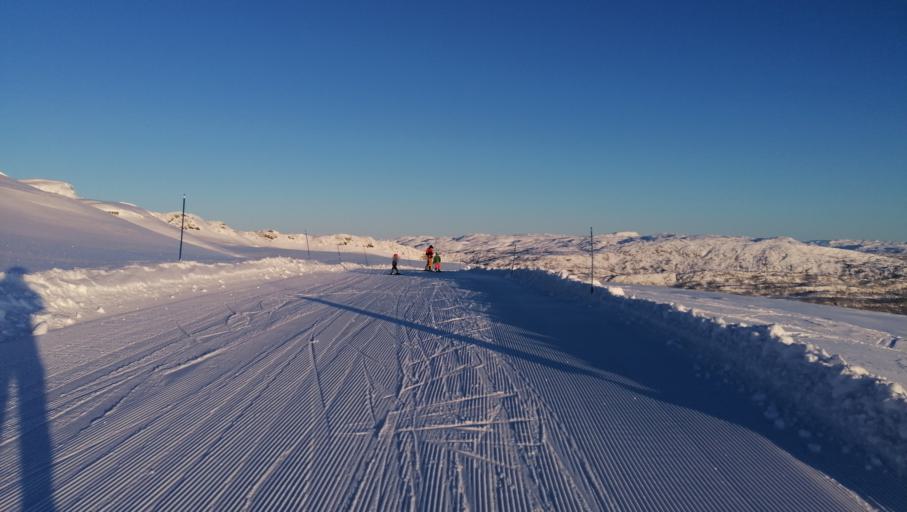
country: NO
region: Aust-Agder
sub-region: Bykle
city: Hovden
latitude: 59.5828
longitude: 7.3315
